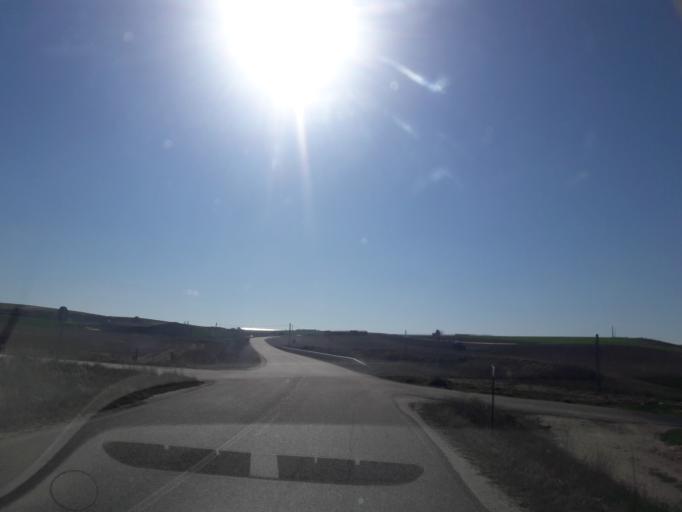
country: ES
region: Castille and Leon
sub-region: Provincia de Salamanca
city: Tordillos
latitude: 40.8540
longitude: -5.3459
